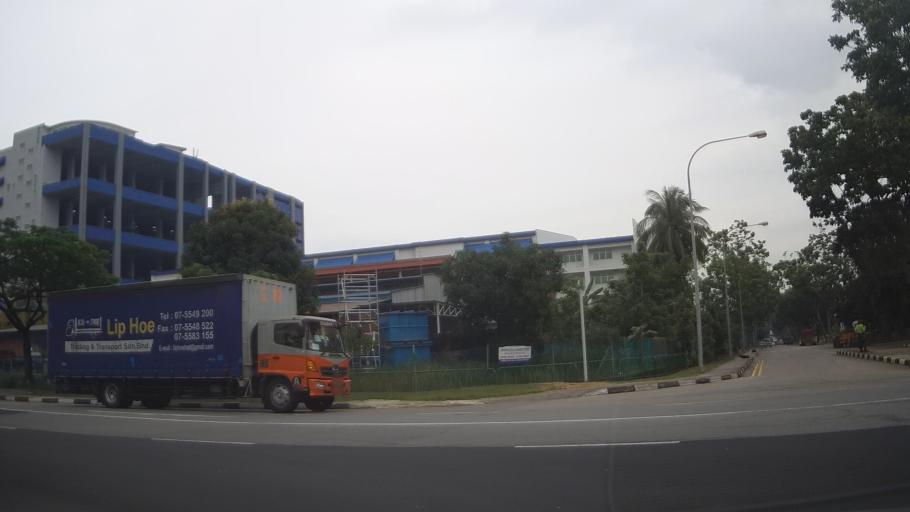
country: MY
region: Johor
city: Johor Bahru
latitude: 1.3173
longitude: 103.6702
